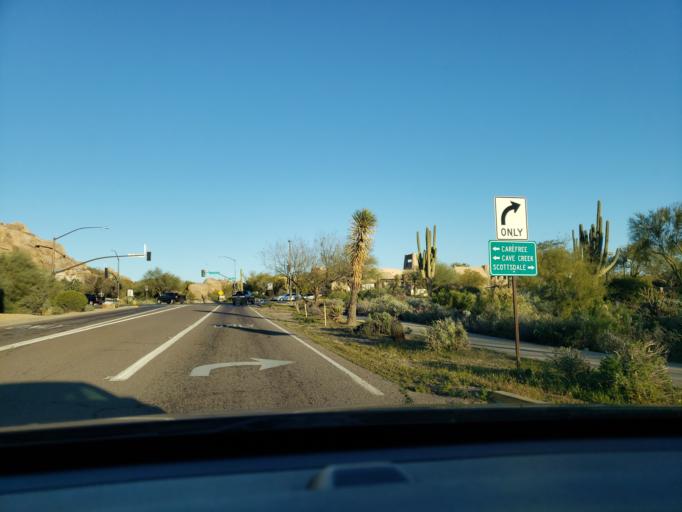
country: US
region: Arizona
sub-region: Maricopa County
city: Carefree
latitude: 33.7992
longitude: -111.9291
